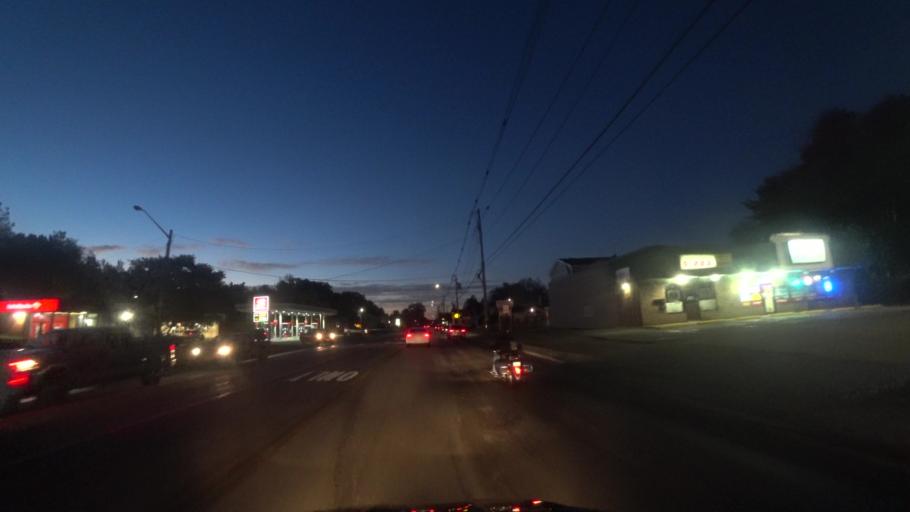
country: US
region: Massachusetts
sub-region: Middlesex County
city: North Reading
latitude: 42.5892
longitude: -71.1165
